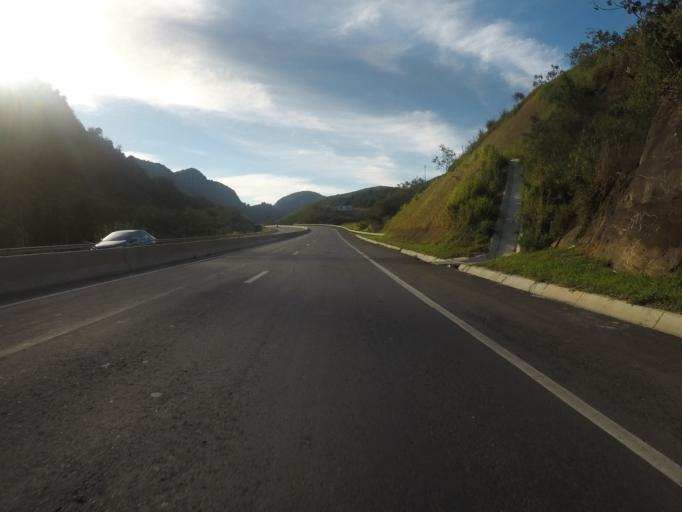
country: BR
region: Espirito Santo
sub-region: Ibiracu
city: Ibiracu
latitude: -19.8508
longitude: -40.3831
